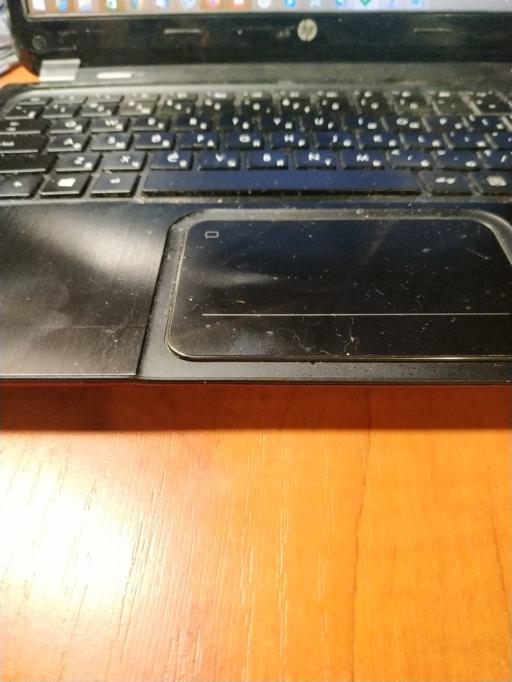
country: RU
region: Orjol
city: Znamenskoye
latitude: 53.1526
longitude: 35.6393
